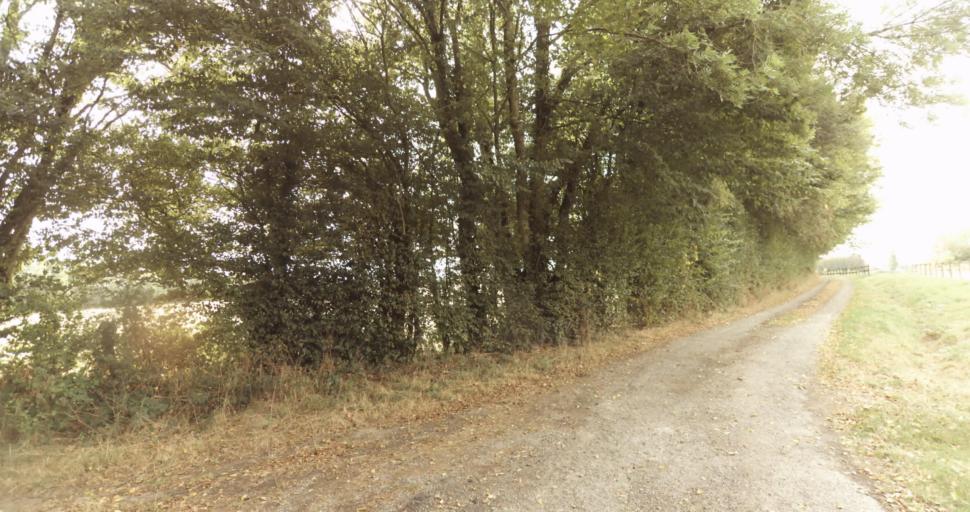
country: FR
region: Lower Normandy
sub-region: Departement de l'Orne
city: Gace
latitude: 48.8860
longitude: 0.3653
